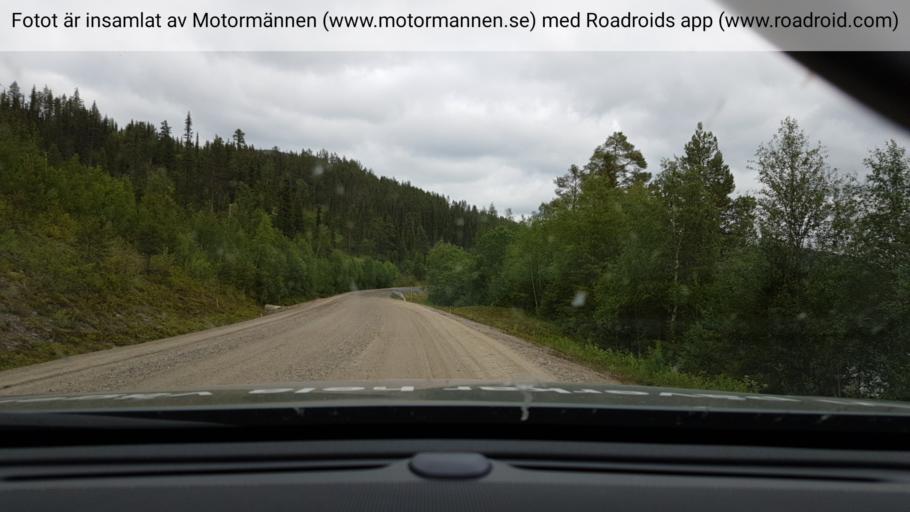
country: SE
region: Vaesterbotten
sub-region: Storumans Kommun
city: Fristad
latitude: 65.8173
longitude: 16.7907
